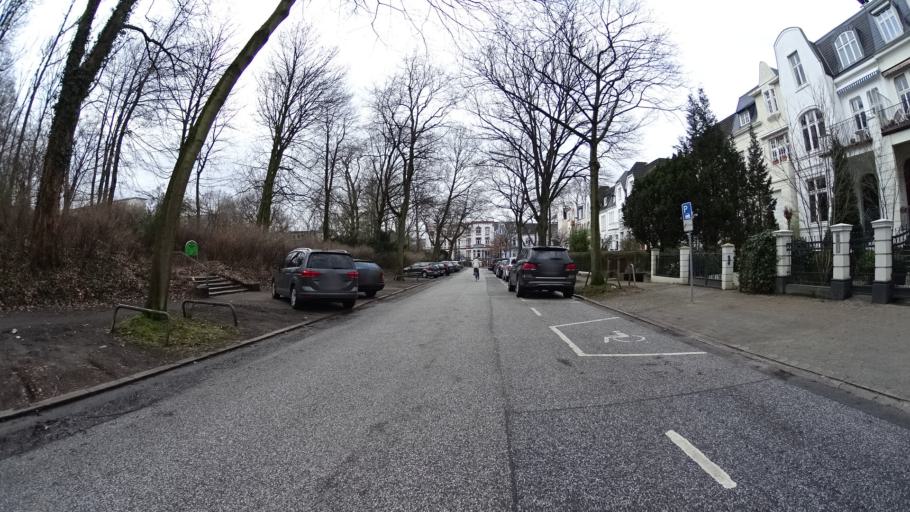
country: DE
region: Hamburg
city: Hamburg-Nord
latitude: 53.5789
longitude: 9.9836
